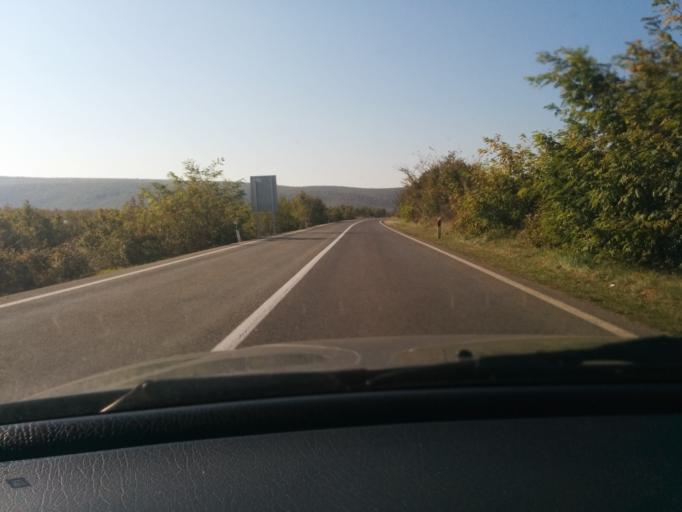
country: HR
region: Splitsko-Dalmatinska
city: Brnaze
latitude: 43.6519
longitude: 16.6367
